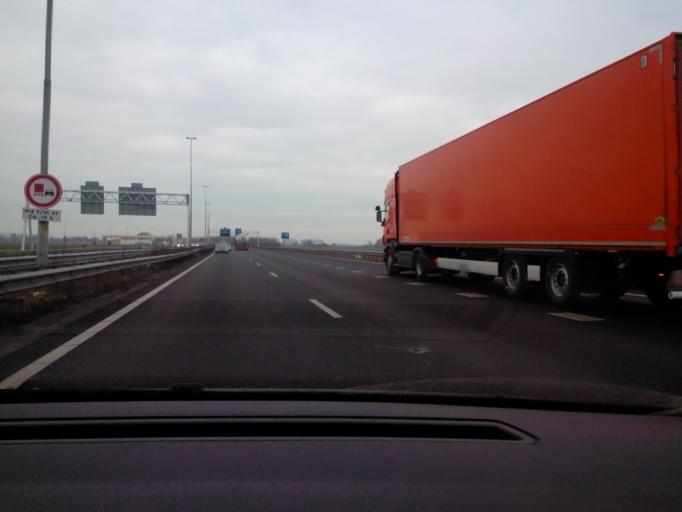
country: NL
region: North Brabant
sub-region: Gemeente Woudrichem
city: Almkerk
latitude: 51.7412
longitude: 4.9154
